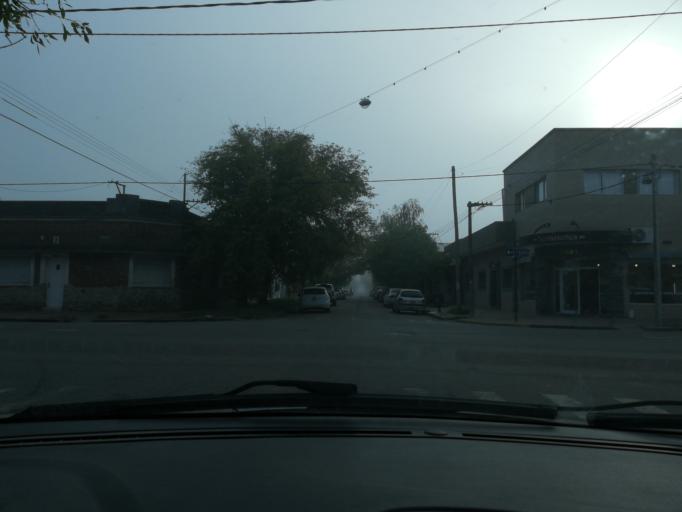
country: AR
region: Buenos Aires
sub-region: Partido de Balcarce
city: Balcarce
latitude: -37.8450
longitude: -58.2516
